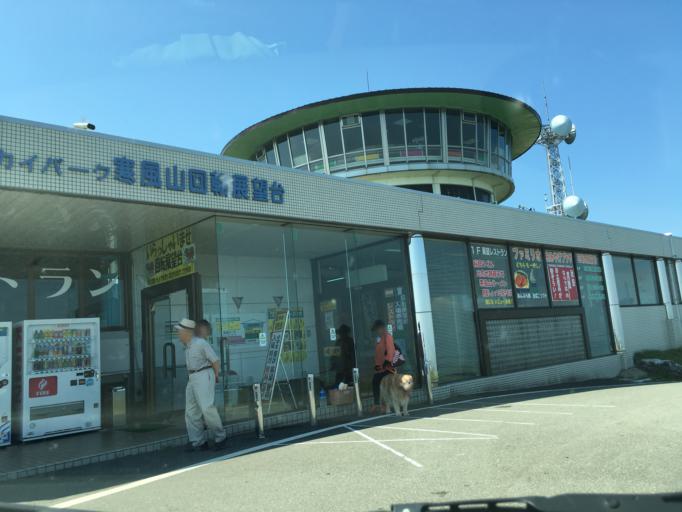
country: JP
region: Akita
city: Tenno
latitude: 39.9336
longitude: 139.8757
